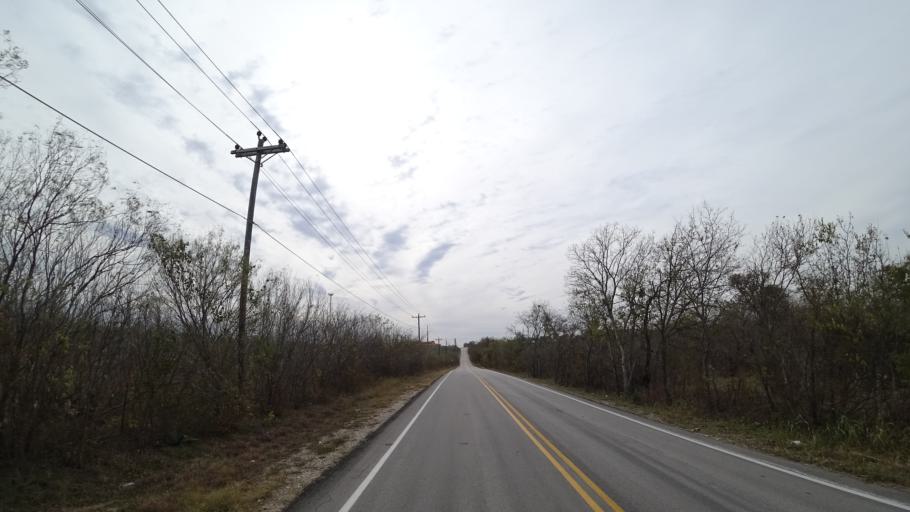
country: US
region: Texas
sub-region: Travis County
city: Garfield
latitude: 30.1440
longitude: -97.5655
